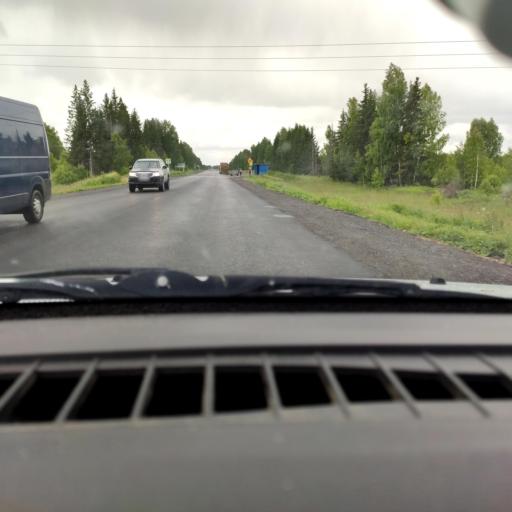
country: RU
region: Perm
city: Orda
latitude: 57.2661
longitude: 57.0178
